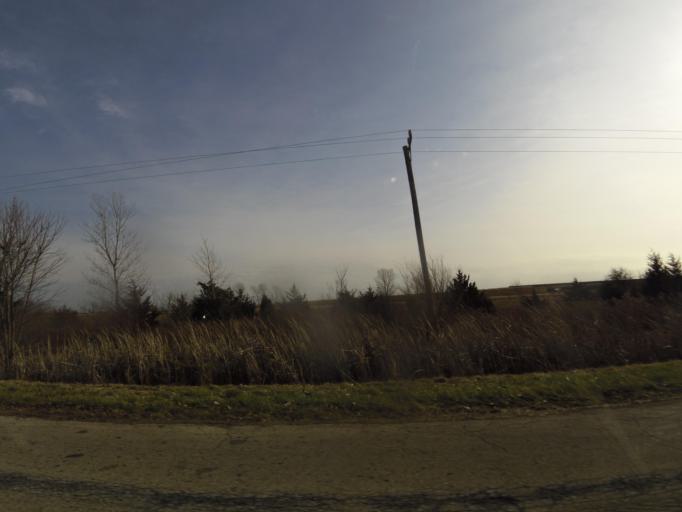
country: US
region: Illinois
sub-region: Macon County
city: Macon
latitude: 39.7673
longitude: -88.9830
